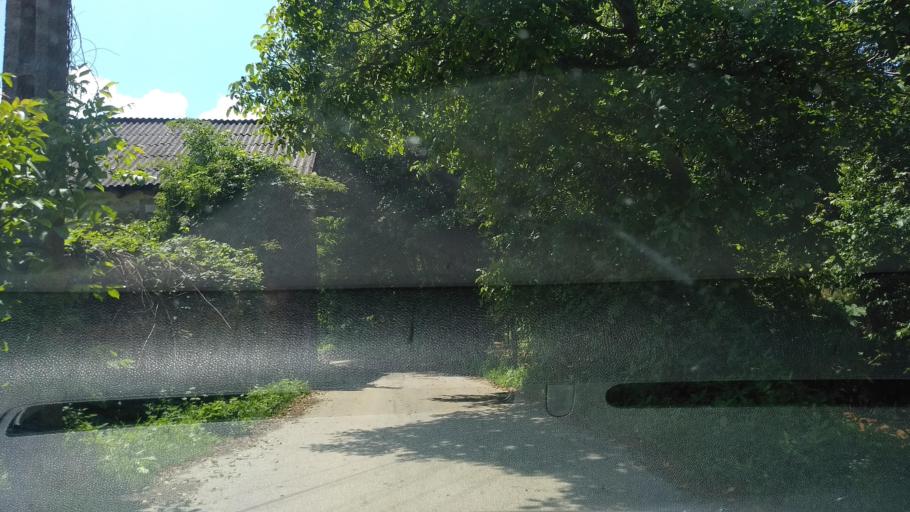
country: RO
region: Hunedoara
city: Densus
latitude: 45.5435
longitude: 22.8186
